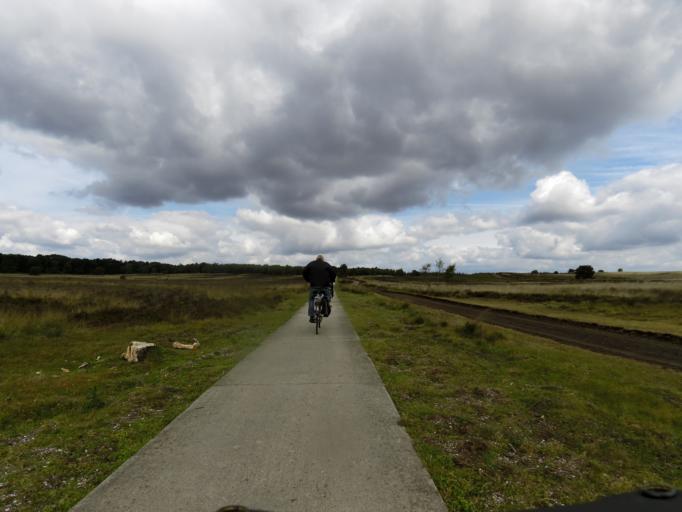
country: NL
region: Gelderland
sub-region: Gemeente Apeldoorn
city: Uddel
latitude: 52.3122
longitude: 5.7657
